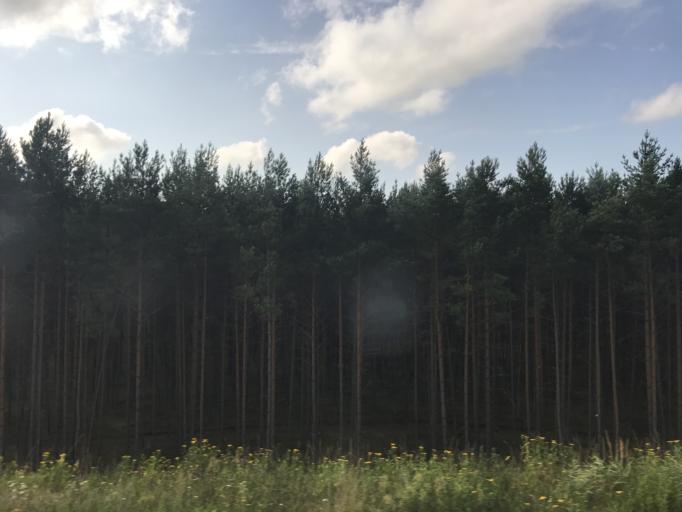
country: PL
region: Kujawsko-Pomorskie
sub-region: Powiat swiecki
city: Warlubie
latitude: 53.5601
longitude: 18.5717
